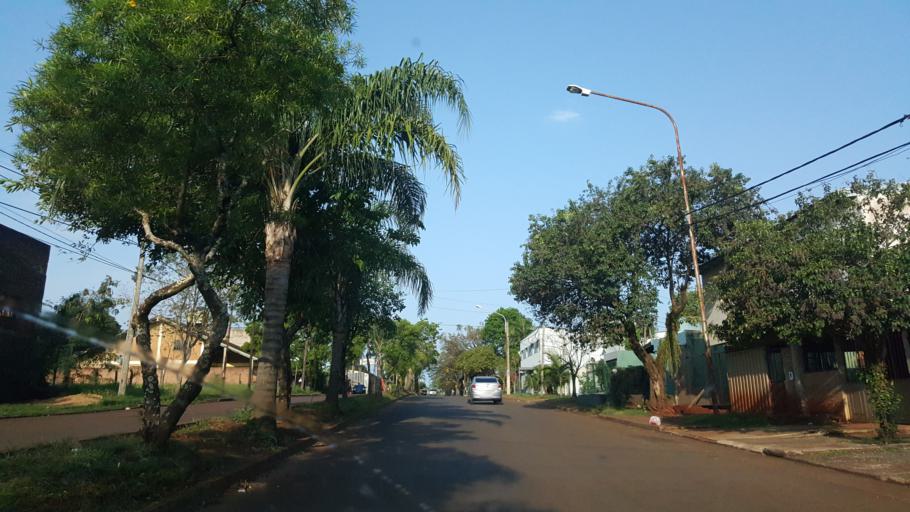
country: AR
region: Misiones
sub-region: Departamento de Capital
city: Posadas
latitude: -27.4014
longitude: -55.9003
